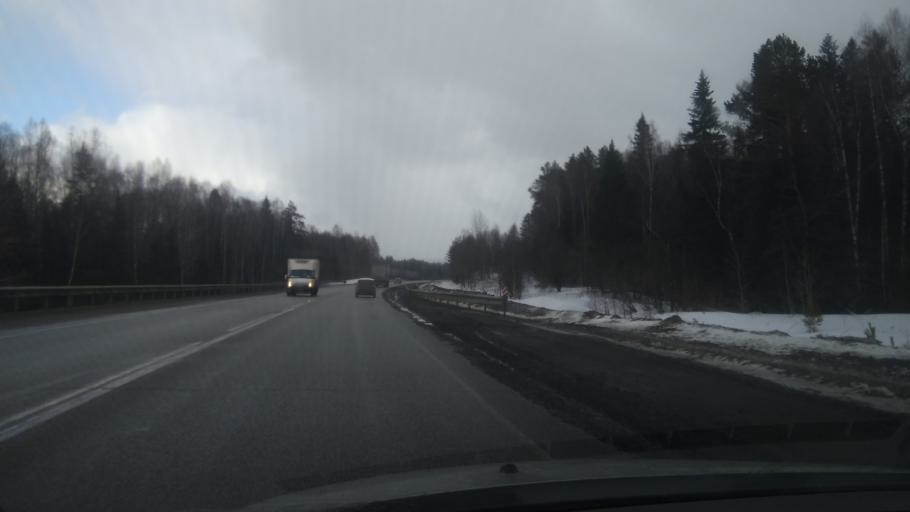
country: RU
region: Sverdlovsk
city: Ufimskiy
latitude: 56.7870
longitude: 58.3827
